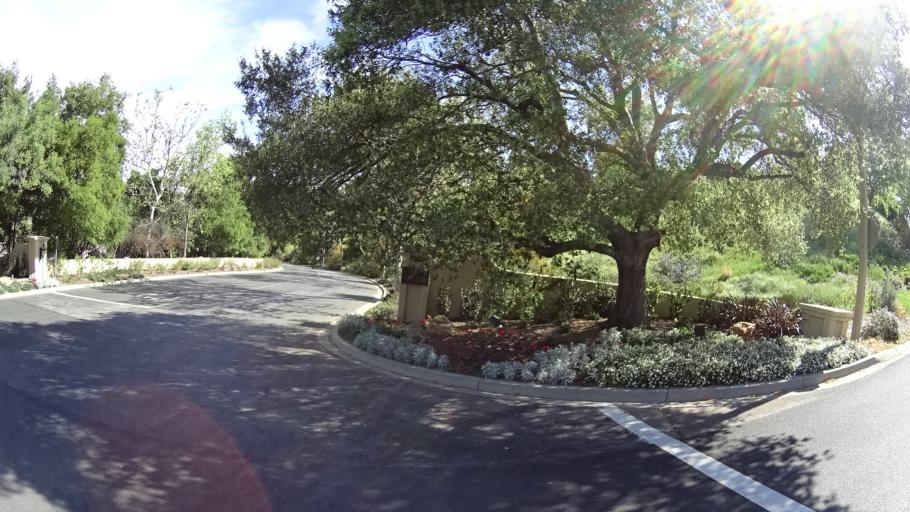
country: US
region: California
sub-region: Ventura County
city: Thousand Oaks
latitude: 34.1891
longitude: -118.8085
